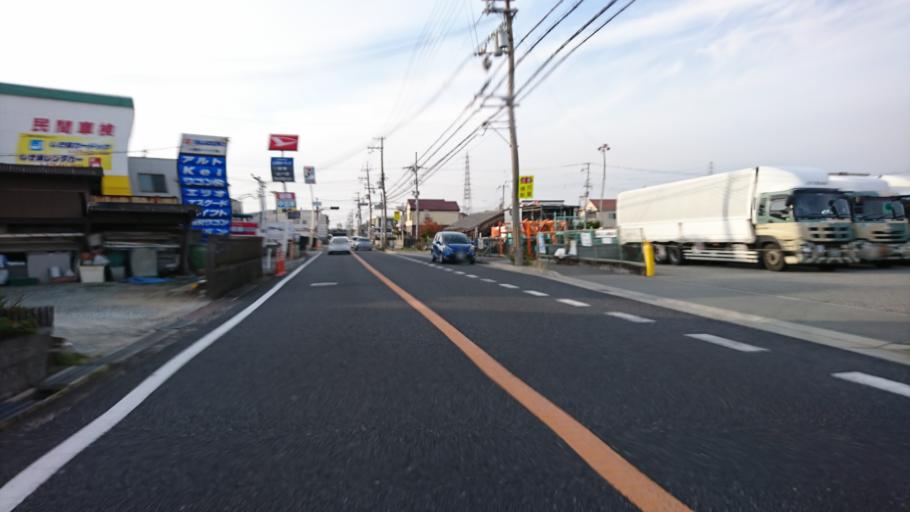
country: JP
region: Hyogo
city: Kakogawacho-honmachi
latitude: 34.7178
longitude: 134.8576
